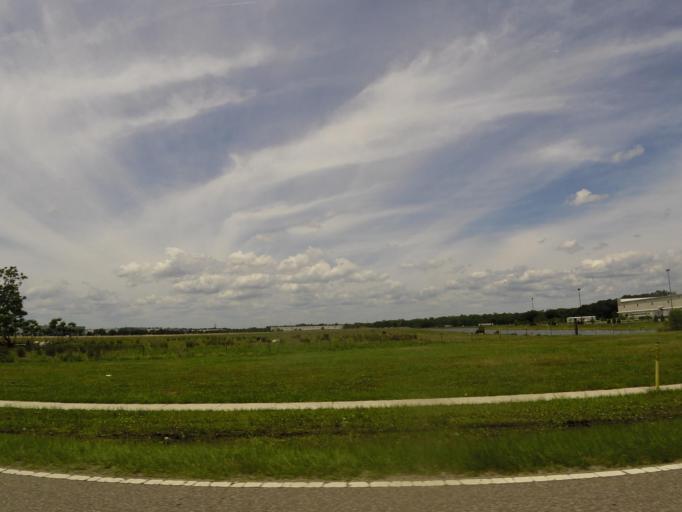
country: US
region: Florida
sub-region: Duval County
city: Jacksonville
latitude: 30.4537
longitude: -81.5581
